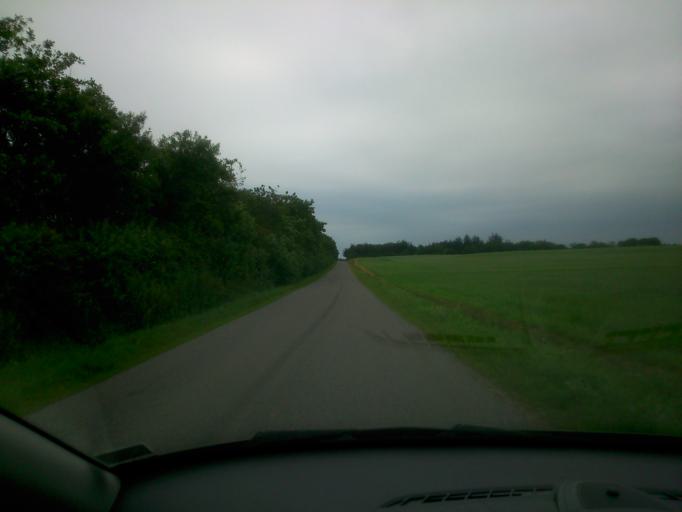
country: DK
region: Central Jutland
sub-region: Ringkobing-Skjern Kommune
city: Skjern
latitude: 55.9777
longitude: 8.4610
